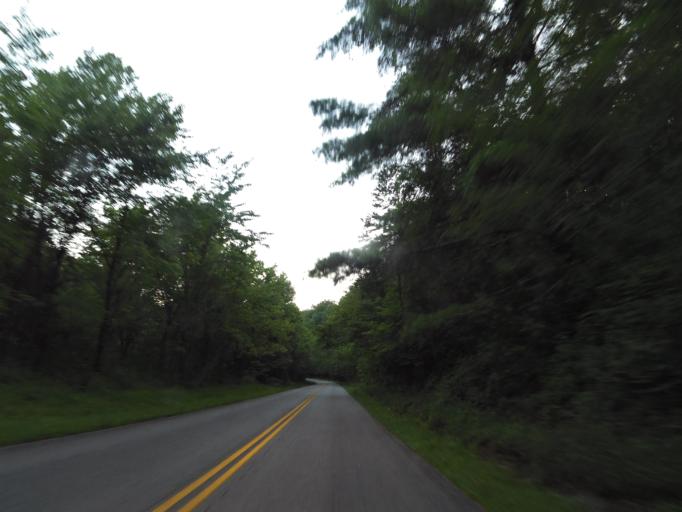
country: US
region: Tennessee
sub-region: Blount County
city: Maryville
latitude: 35.5660
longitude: -84.0038
